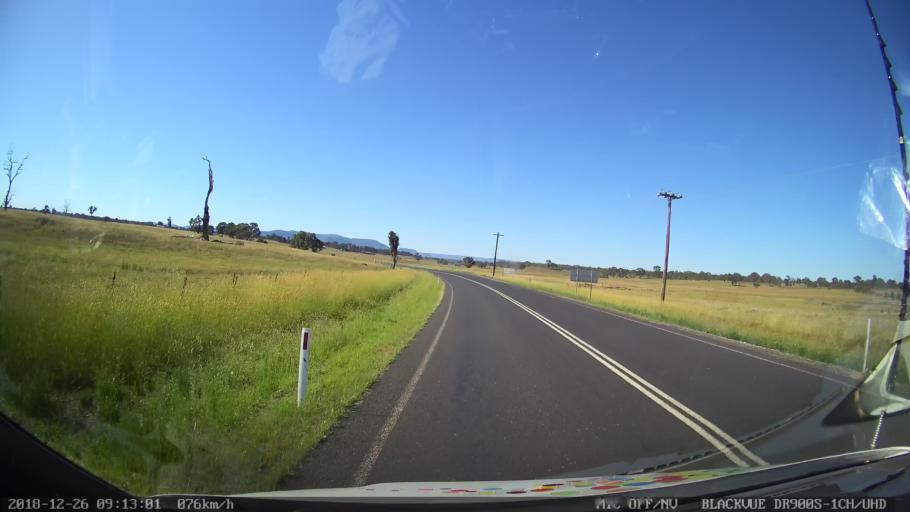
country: AU
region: New South Wales
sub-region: Mid-Western Regional
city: Kandos
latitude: -32.7633
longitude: 149.9783
